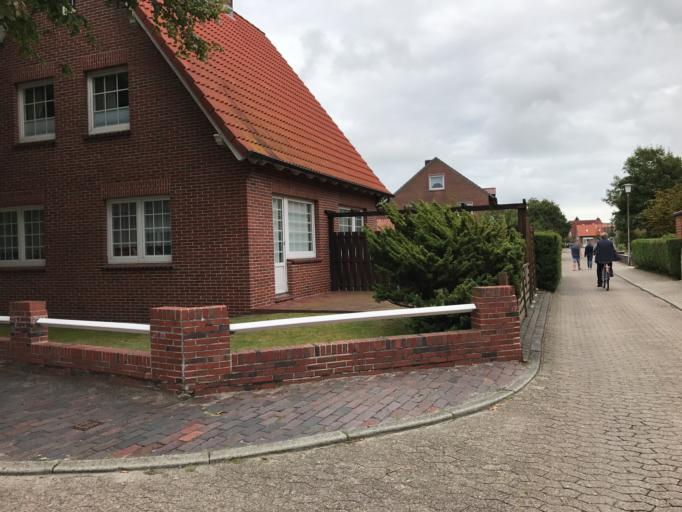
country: DE
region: Lower Saxony
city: Borkum
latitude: 53.5861
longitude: 6.6693
